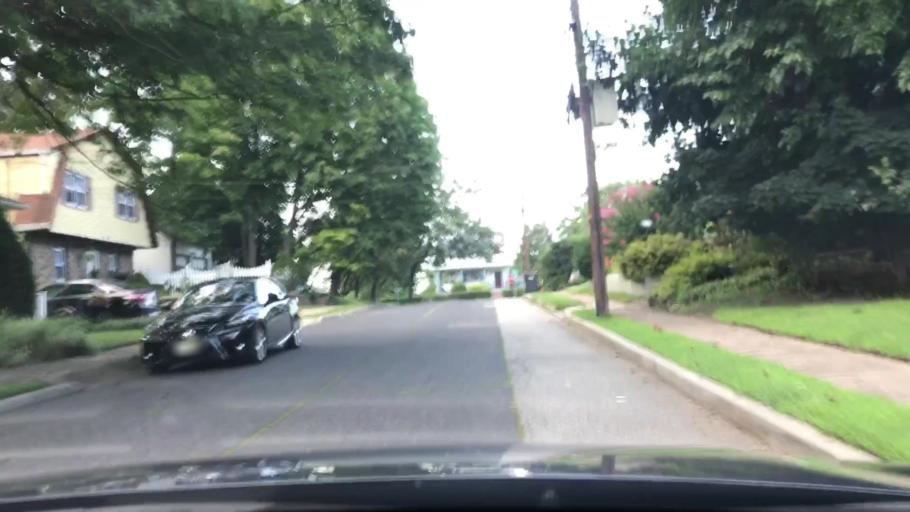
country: US
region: New Jersey
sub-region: Bergen County
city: Bergenfield
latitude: 40.9324
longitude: -74.0000
